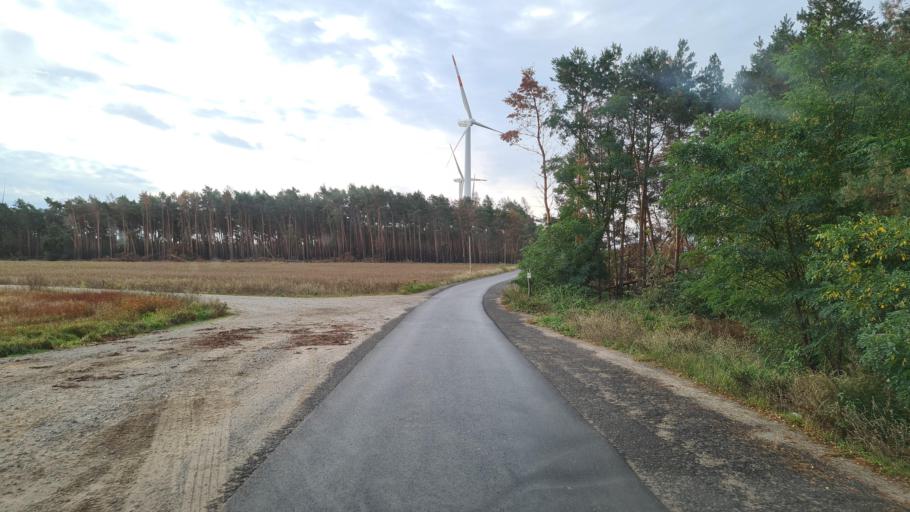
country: DE
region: Brandenburg
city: Kasel-Golzig
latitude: 51.9225
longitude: 13.7481
